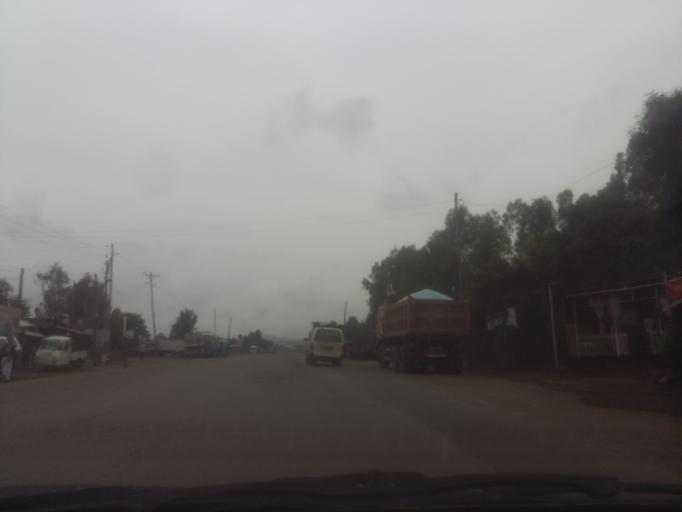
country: ET
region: Oromiya
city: Bishoftu
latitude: 8.7964
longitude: 38.8985
